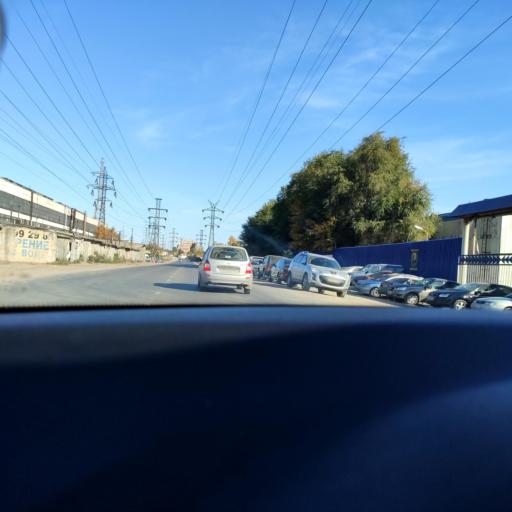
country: RU
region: Samara
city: Petra-Dubrava
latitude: 53.2411
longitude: 50.2897
